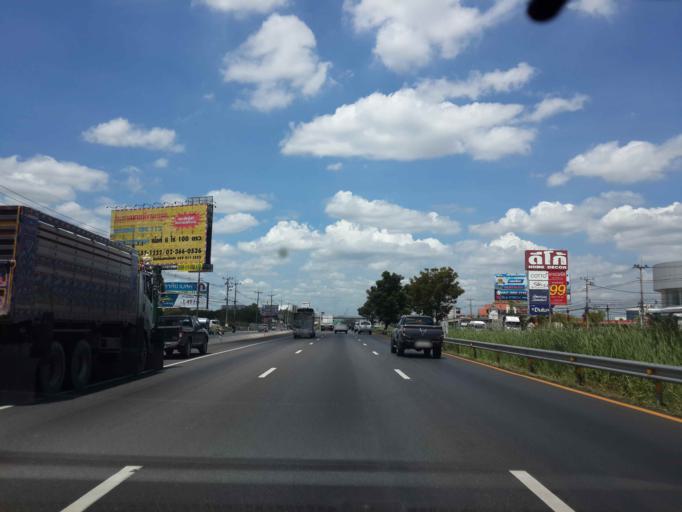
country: TH
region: Bangkok
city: Bang Bon
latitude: 13.6018
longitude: 100.3692
